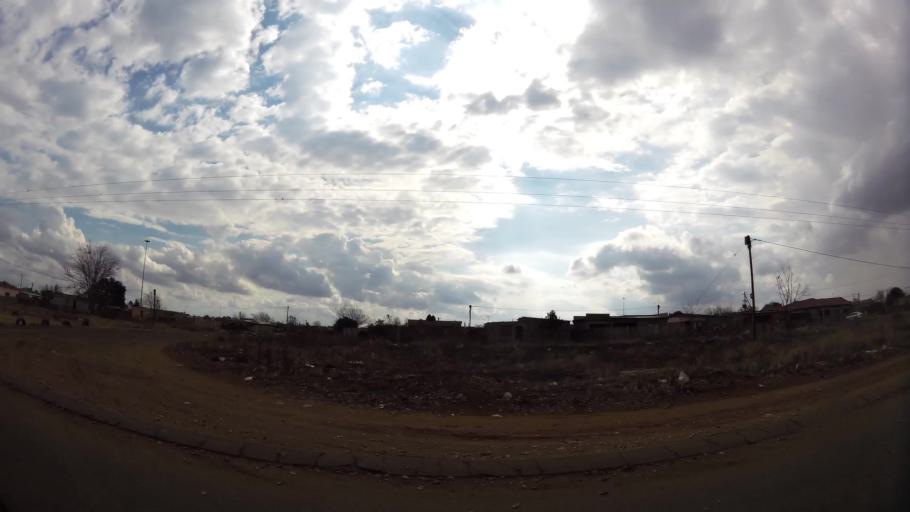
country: ZA
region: Gauteng
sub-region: Sedibeng District Municipality
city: Vanderbijlpark
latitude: -26.7039
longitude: 27.8033
